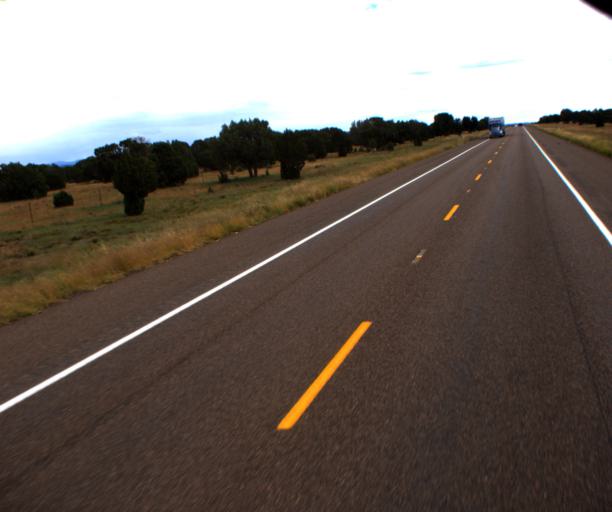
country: US
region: Arizona
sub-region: Navajo County
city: Show Low
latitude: 34.2998
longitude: -110.0348
